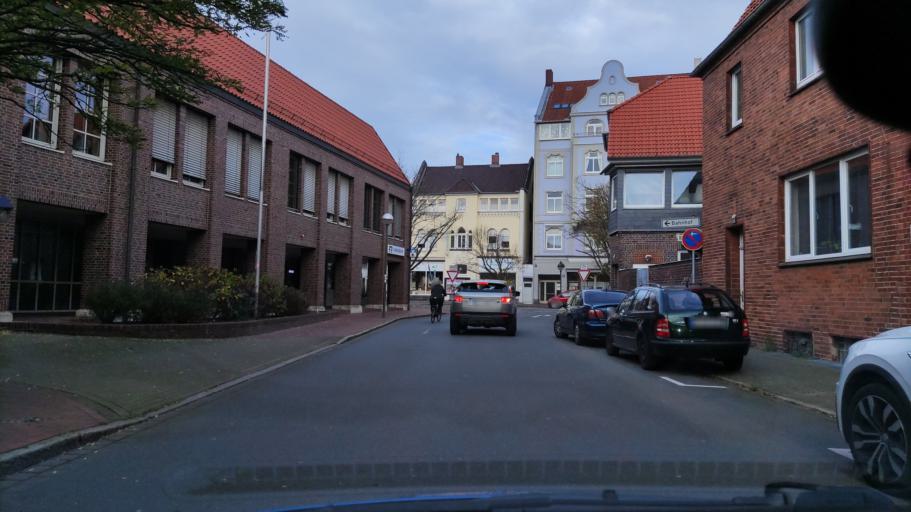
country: DE
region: Lower Saxony
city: Uelzen
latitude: 52.9658
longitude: 10.5553
